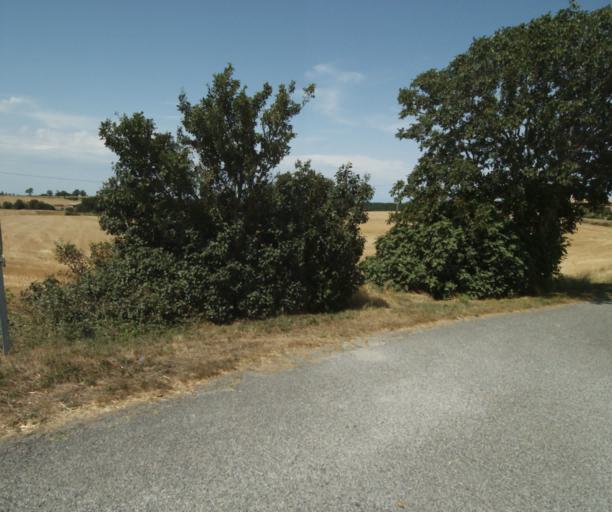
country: FR
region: Midi-Pyrenees
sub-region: Departement de la Haute-Garonne
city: Saint-Felix-Lauragais
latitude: 43.4599
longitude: 1.8489
